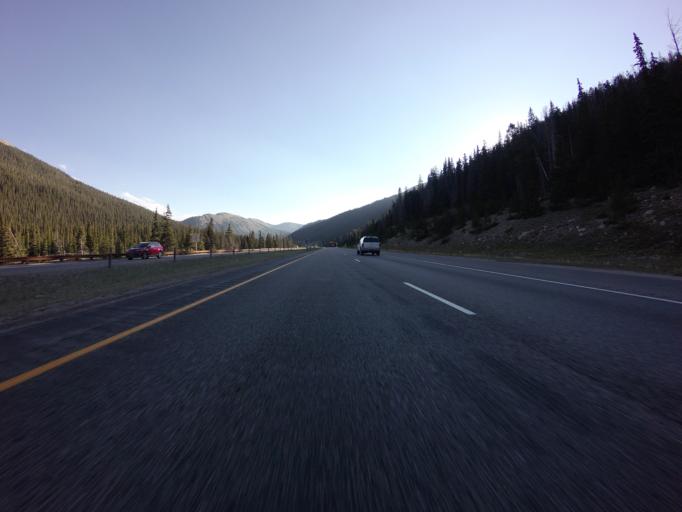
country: US
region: Colorado
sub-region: Summit County
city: Keystone
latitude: 39.6983
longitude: -105.8697
